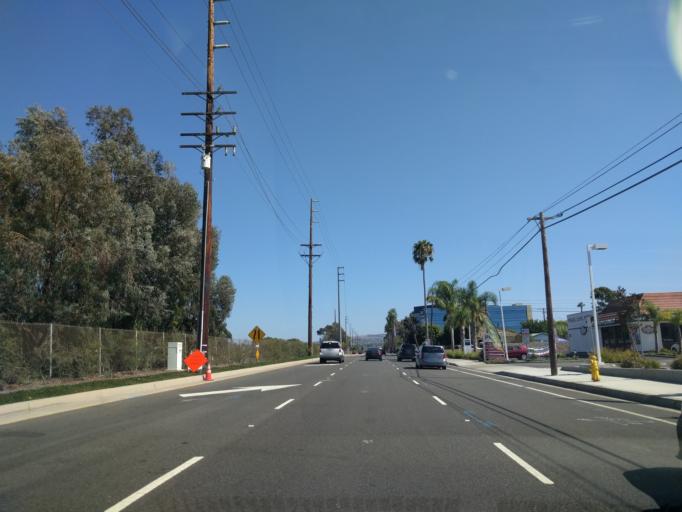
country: US
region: California
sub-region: Orange County
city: Irvine
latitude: 33.6595
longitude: -117.8719
